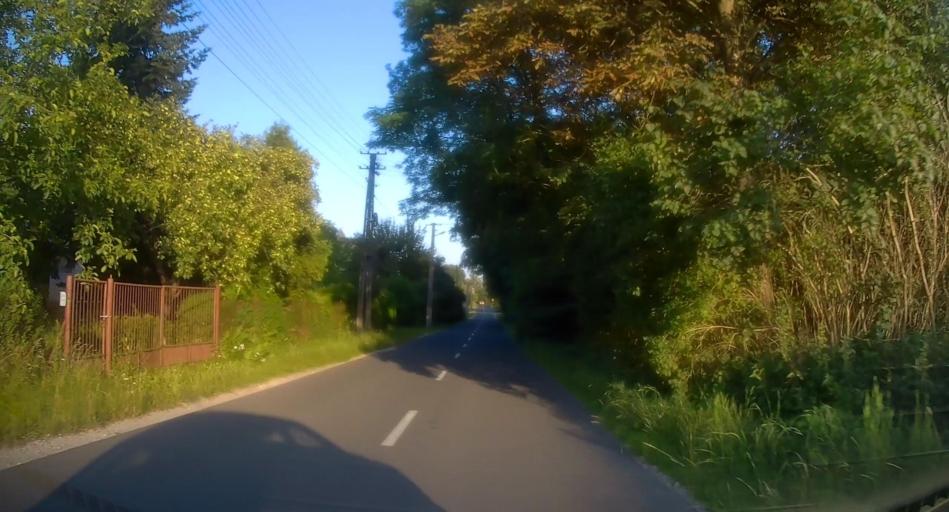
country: PL
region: Lodz Voivodeship
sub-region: Powiat skierniewicki
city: Kowiesy
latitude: 51.8996
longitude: 20.3717
